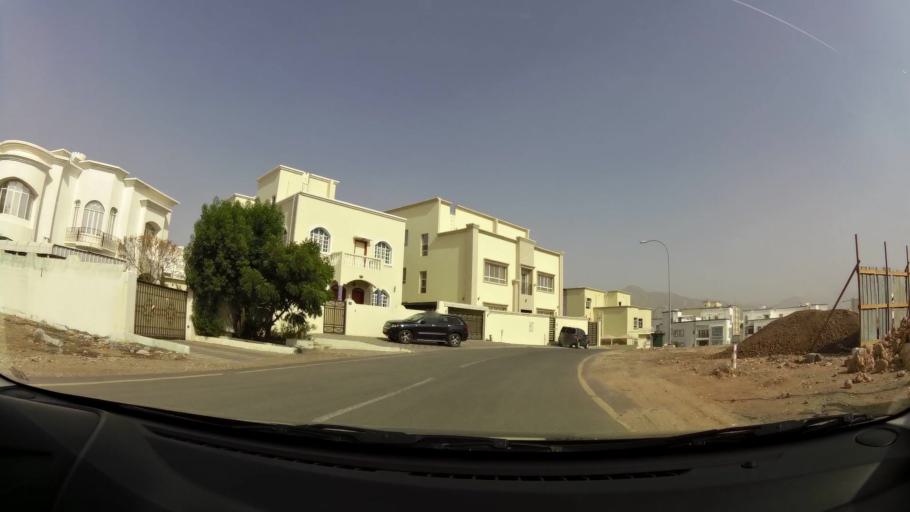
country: OM
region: Muhafazat Masqat
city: Bawshar
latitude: 23.5606
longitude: 58.3609
